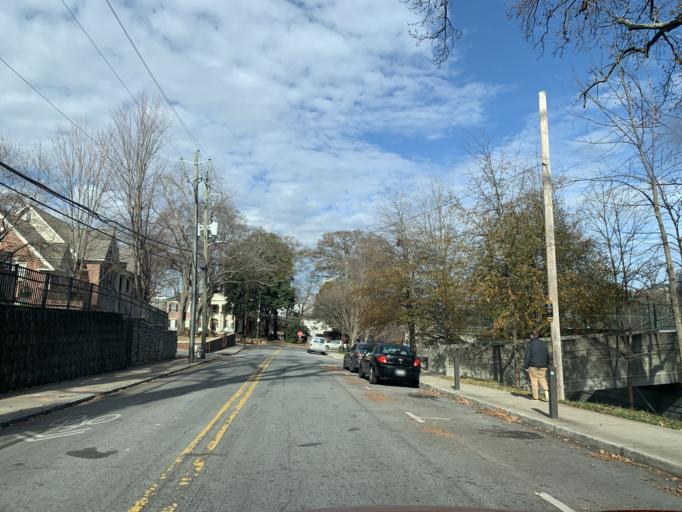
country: US
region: Georgia
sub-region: Fulton County
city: Atlanta
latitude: 33.7750
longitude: -84.3940
